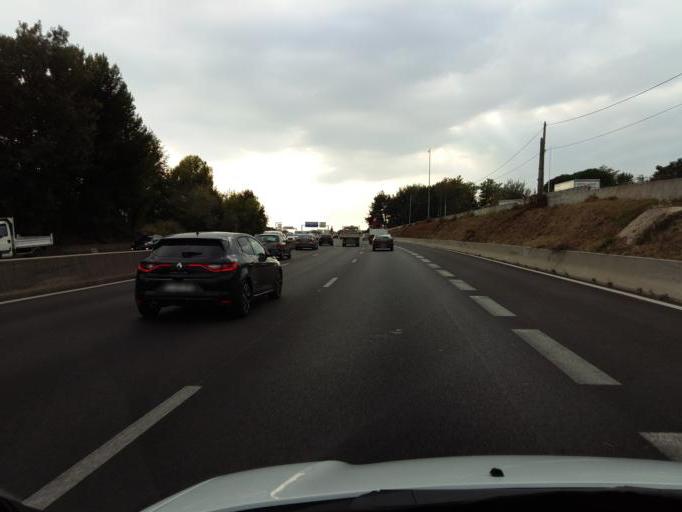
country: FR
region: Provence-Alpes-Cote d'Azur
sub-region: Departement des Bouches-du-Rhone
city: Cabries
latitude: 43.4259
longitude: 5.3784
